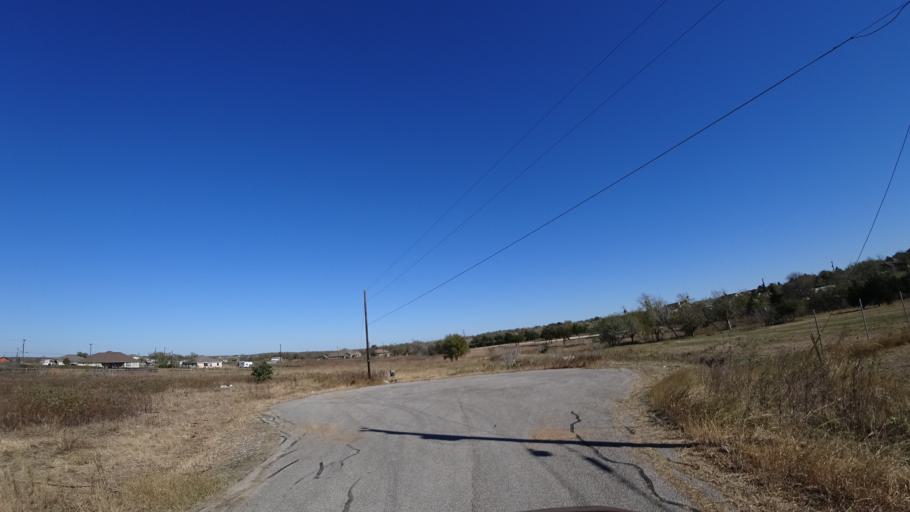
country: US
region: Texas
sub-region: Travis County
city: Garfield
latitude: 30.1018
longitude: -97.6032
